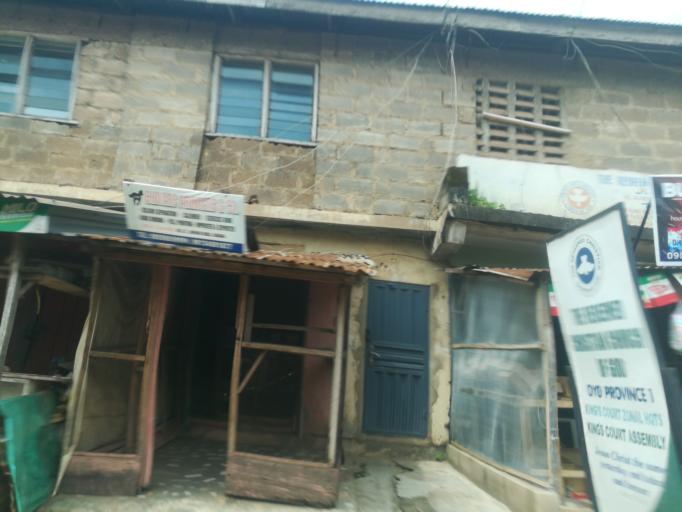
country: NG
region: Oyo
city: Ibadan
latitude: 7.3587
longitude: 3.8811
